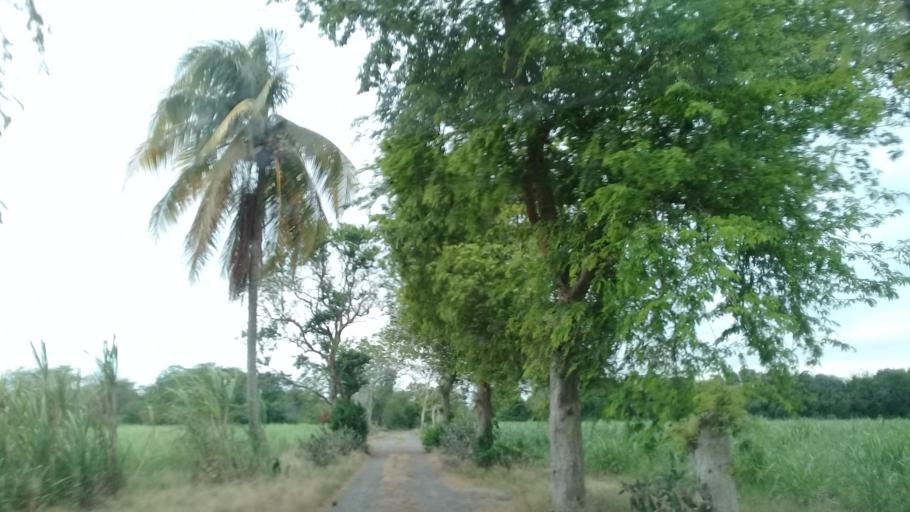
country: MX
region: Veracruz
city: Ursulo Galvan
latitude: 19.3833
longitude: -96.3607
